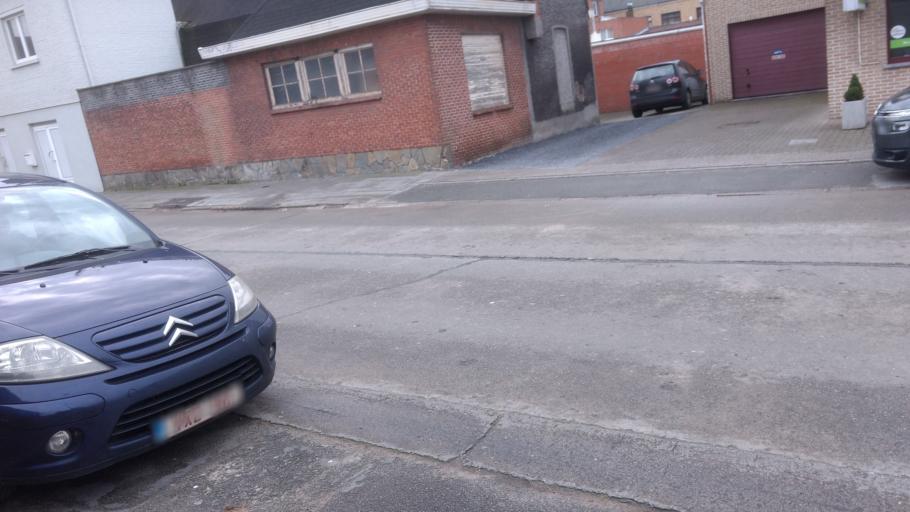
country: BE
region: Flanders
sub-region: Provincie Oost-Vlaanderen
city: Lochristi
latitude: 51.0965
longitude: 3.8317
